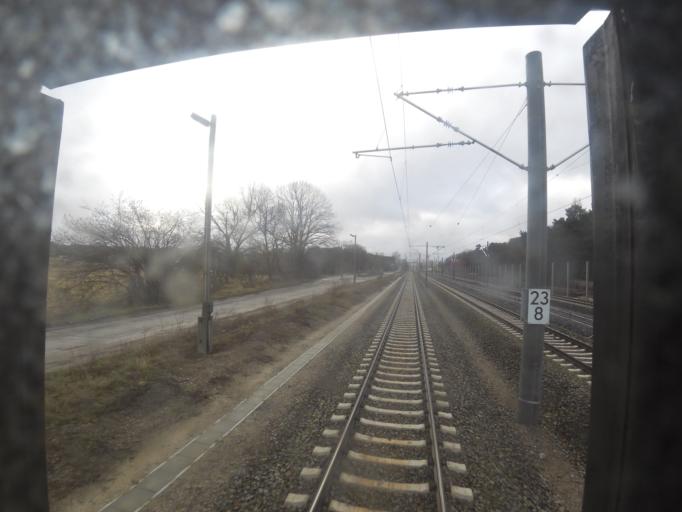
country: DE
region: Brandenburg
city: Rangsdorf
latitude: 52.2987
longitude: 13.4293
